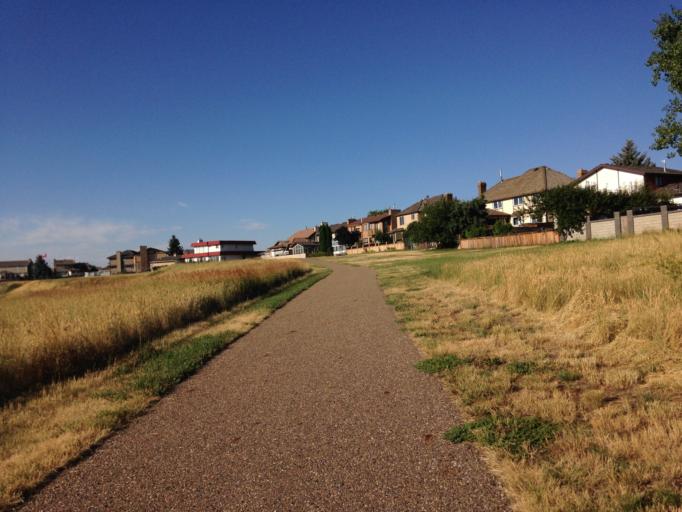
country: CA
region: Alberta
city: Medicine Hat
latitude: 49.9993
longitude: -110.6241
